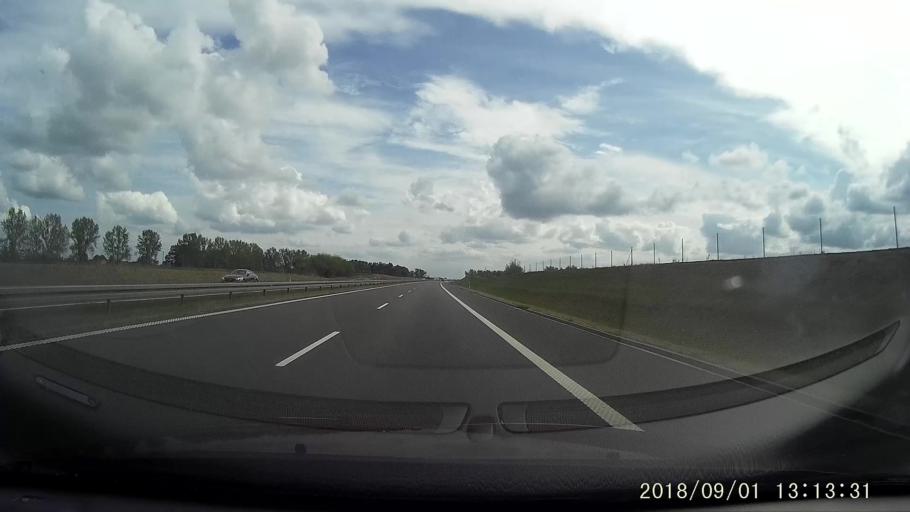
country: PL
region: West Pomeranian Voivodeship
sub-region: Powiat gryfinski
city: Gryfino
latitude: 53.2892
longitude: 14.6047
